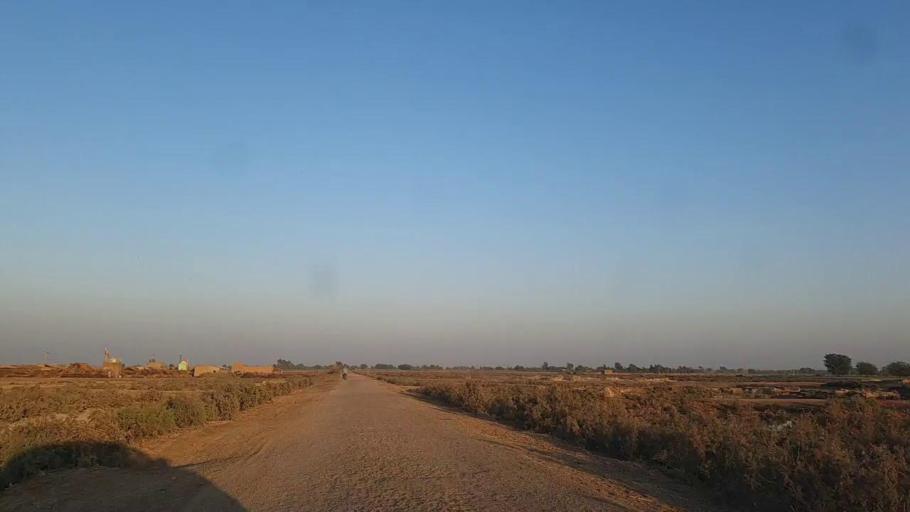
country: PK
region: Sindh
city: Samaro
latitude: 25.2977
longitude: 69.3875
